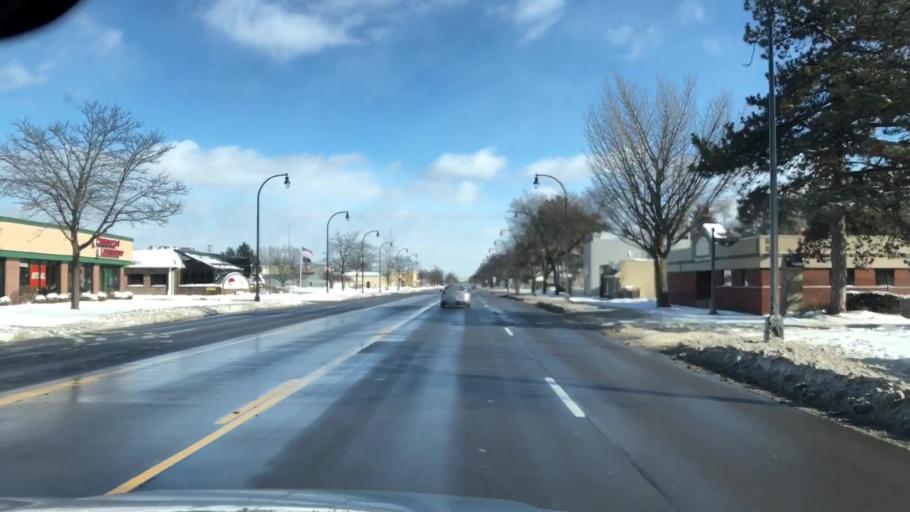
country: US
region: Michigan
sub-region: Wayne County
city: Livonia
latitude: 42.3685
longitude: -83.3604
